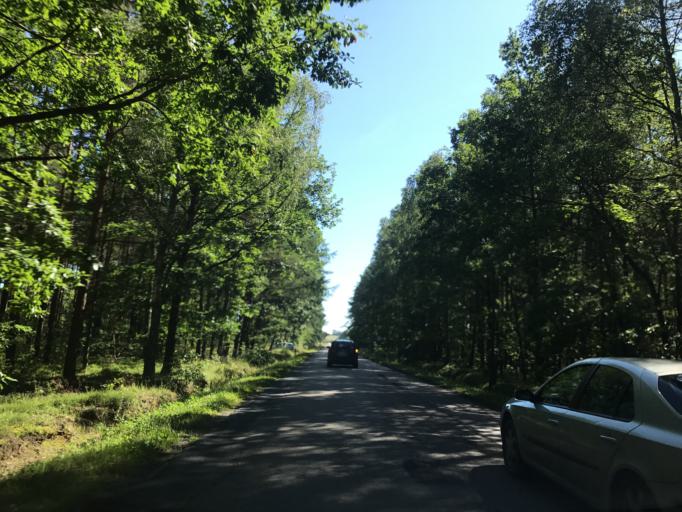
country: PL
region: Pomeranian Voivodeship
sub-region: Powiat bytowski
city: Czarna Dabrowka
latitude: 54.3406
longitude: 17.6618
